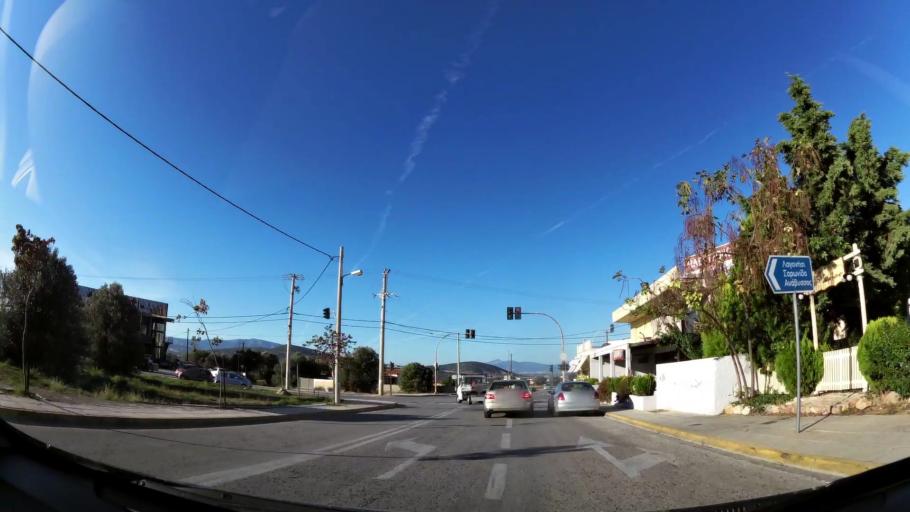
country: GR
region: Attica
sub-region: Nomarchia Anatolikis Attikis
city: Kalyvia Thorikou
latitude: 37.8378
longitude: 23.9229
